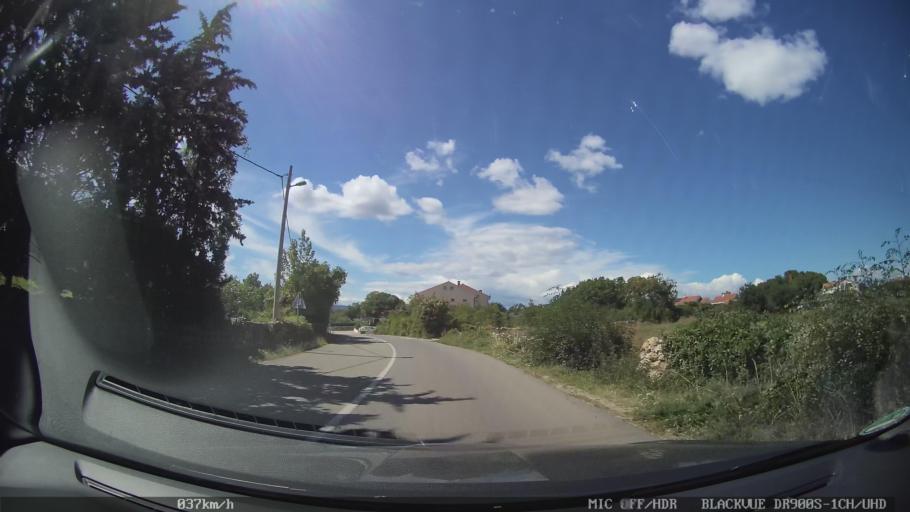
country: HR
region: Primorsko-Goranska
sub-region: Grad Krk
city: Krk
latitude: 45.0509
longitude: 14.5236
